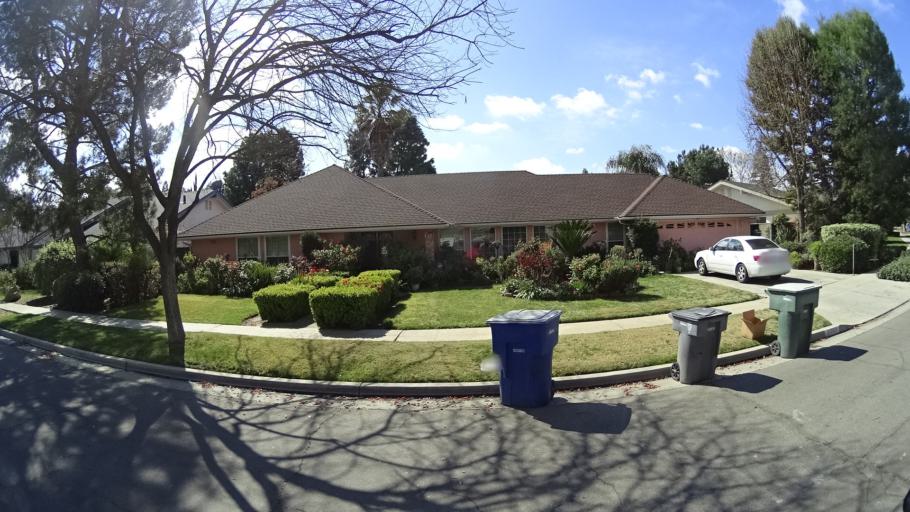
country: US
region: California
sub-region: Fresno County
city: Fresno
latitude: 36.8330
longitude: -119.8500
